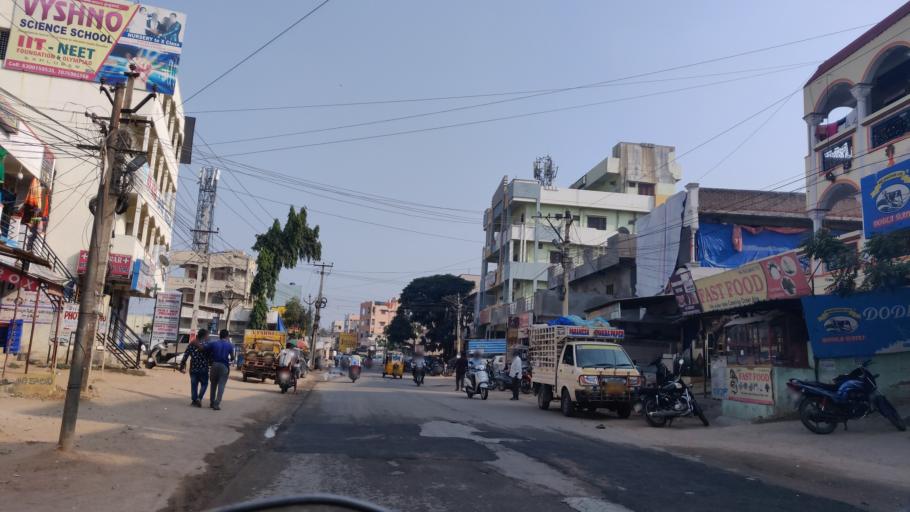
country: IN
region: Telangana
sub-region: Rangareddi
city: Uppal Kalan
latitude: 17.3960
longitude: 78.5909
